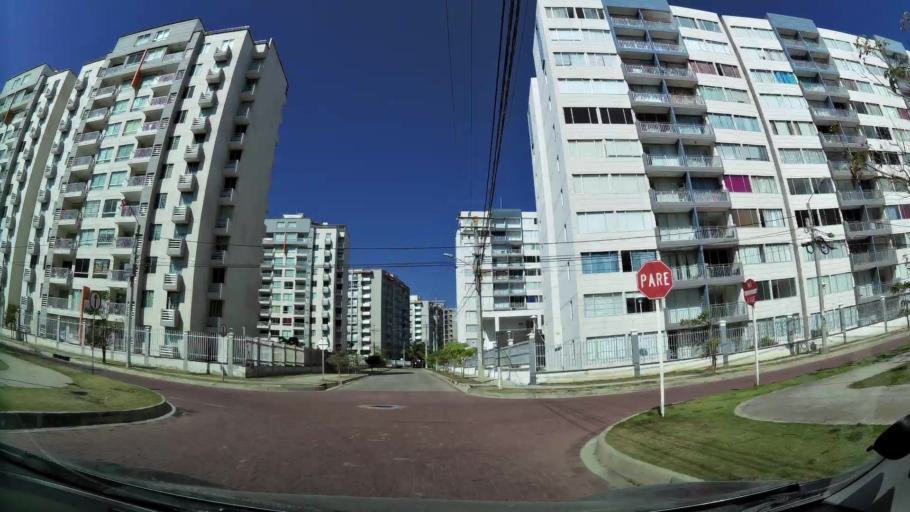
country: CO
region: Atlantico
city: Barranquilla
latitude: 11.0224
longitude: -74.8161
